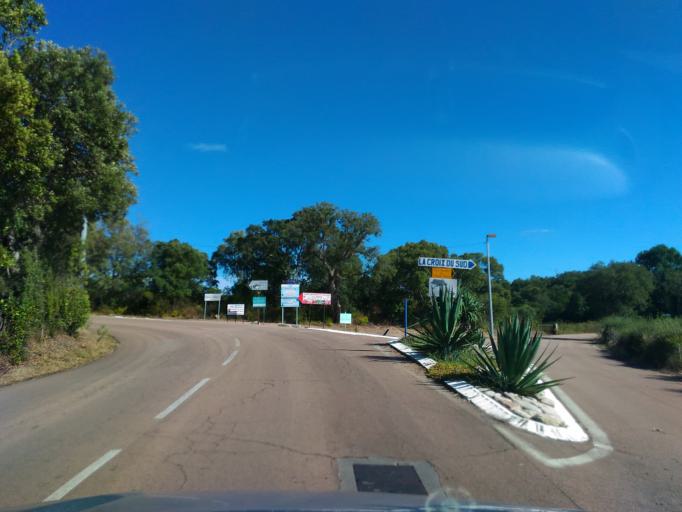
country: FR
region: Corsica
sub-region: Departement de la Corse-du-Sud
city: Porto-Vecchio
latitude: 41.6939
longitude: 9.3699
